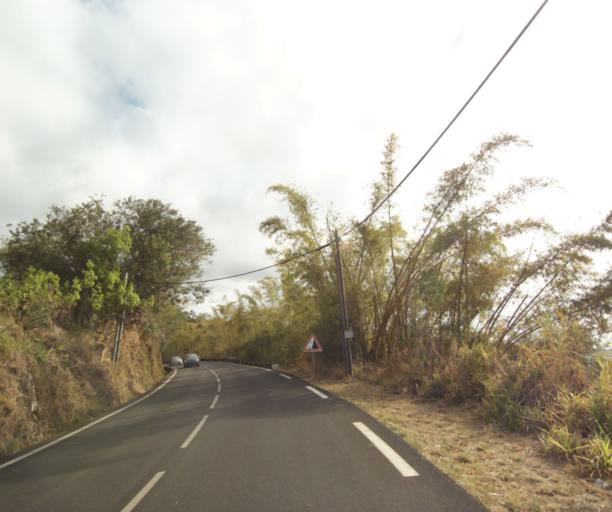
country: RE
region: Reunion
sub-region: Reunion
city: Saint-Paul
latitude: -21.0158
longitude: 55.3184
